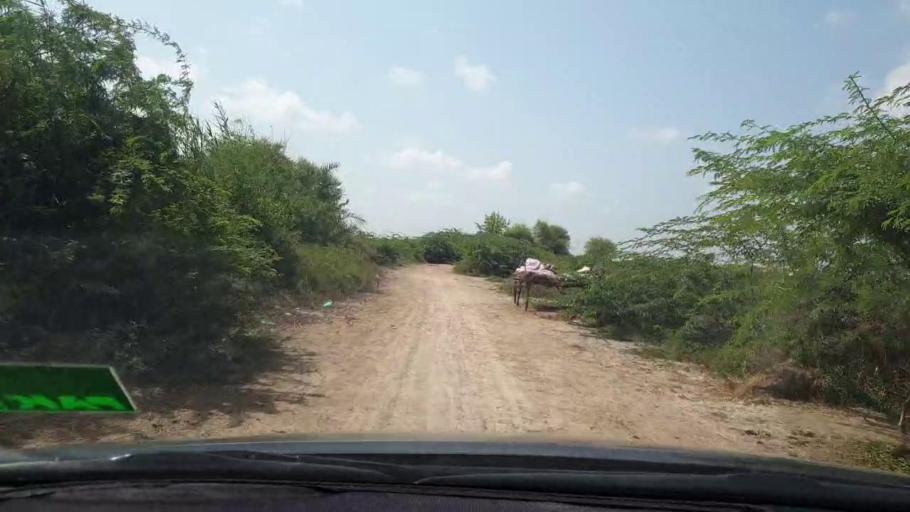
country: PK
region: Sindh
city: Tando Bago
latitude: 24.9349
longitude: 69.0462
